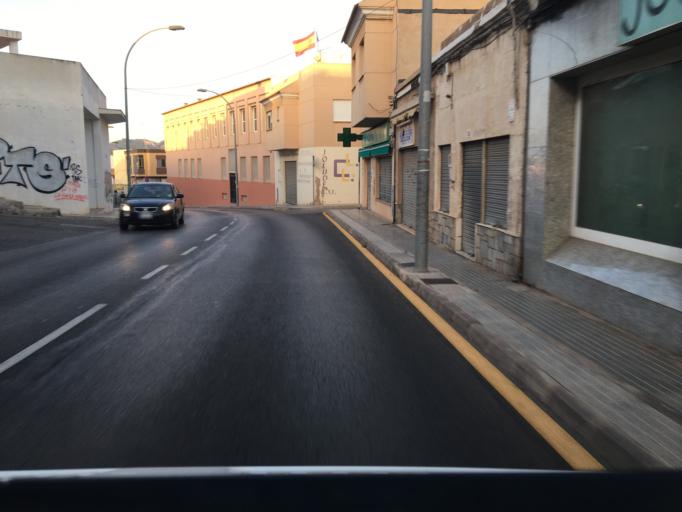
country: ES
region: Murcia
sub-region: Murcia
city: Cartagena
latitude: 37.6270
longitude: -0.9885
